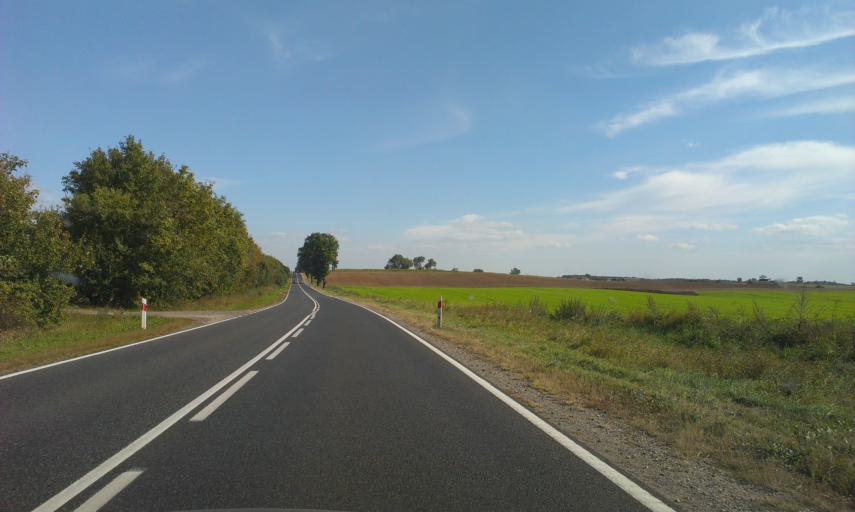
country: PL
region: Kujawsko-Pomorskie
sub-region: Powiat nakielski
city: Sadki
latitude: 53.1555
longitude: 17.4689
